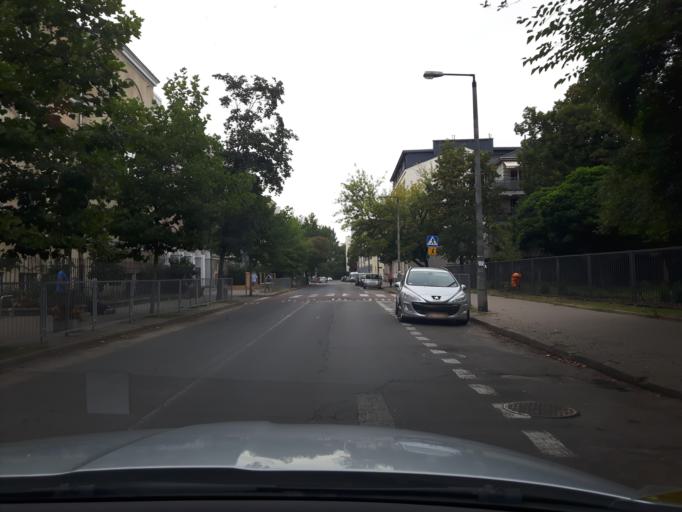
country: PL
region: Masovian Voivodeship
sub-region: Warszawa
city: Praga Polnoc
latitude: 52.2591
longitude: 21.0581
